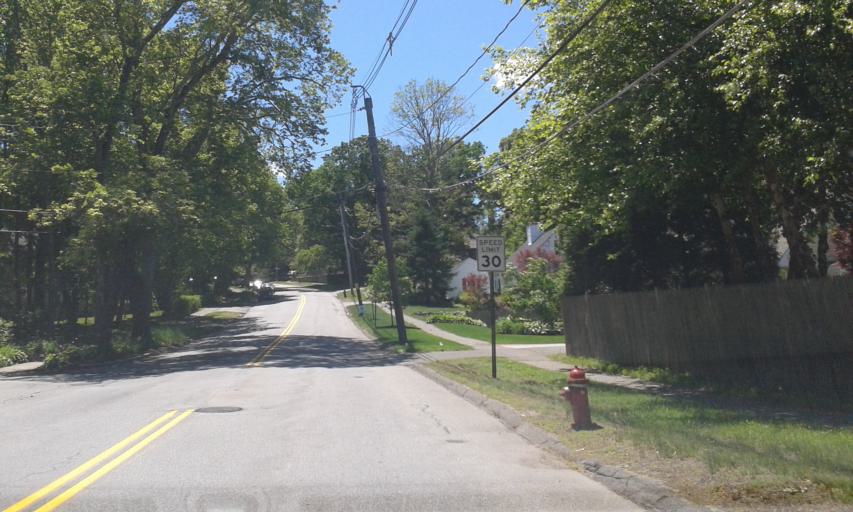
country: US
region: Massachusetts
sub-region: Middlesex County
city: Winchester
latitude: 42.4683
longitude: -71.1207
